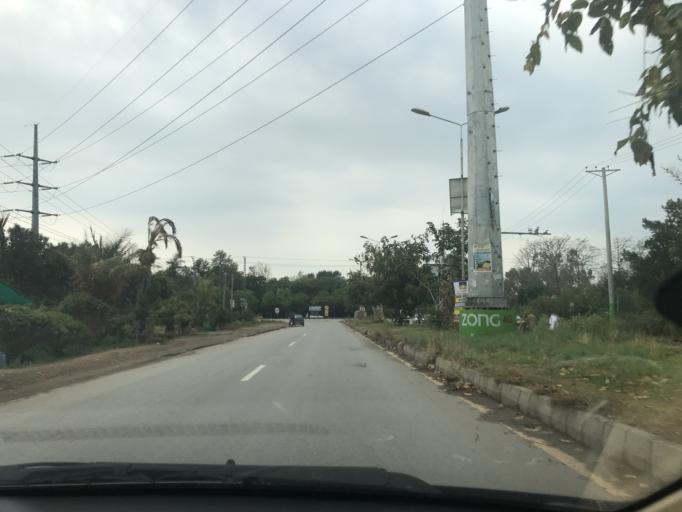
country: PK
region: Punjab
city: Rawalpindi
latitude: 33.6750
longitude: 73.1453
